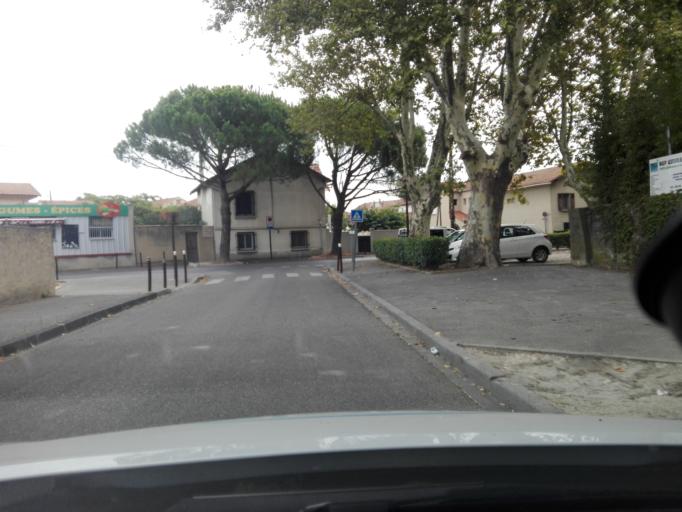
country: FR
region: Provence-Alpes-Cote d'Azur
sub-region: Departement du Vaucluse
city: Avignon
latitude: 43.9358
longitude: 4.8260
